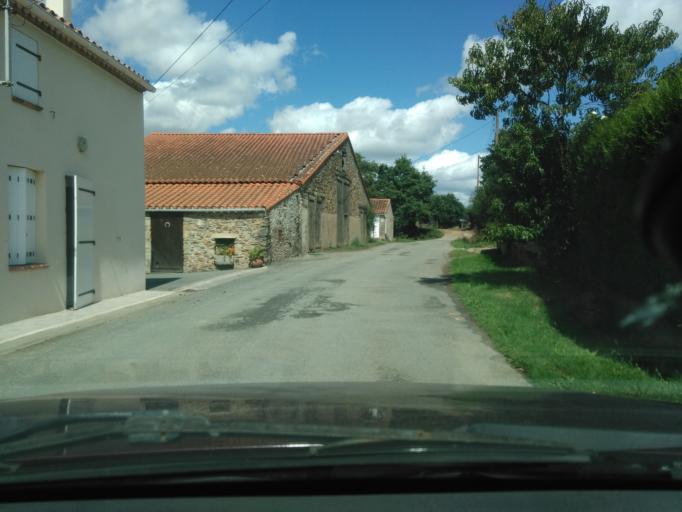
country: FR
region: Pays de la Loire
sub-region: Departement de la Vendee
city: Dompierre-sur-Yon
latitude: 46.7334
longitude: -1.3700
